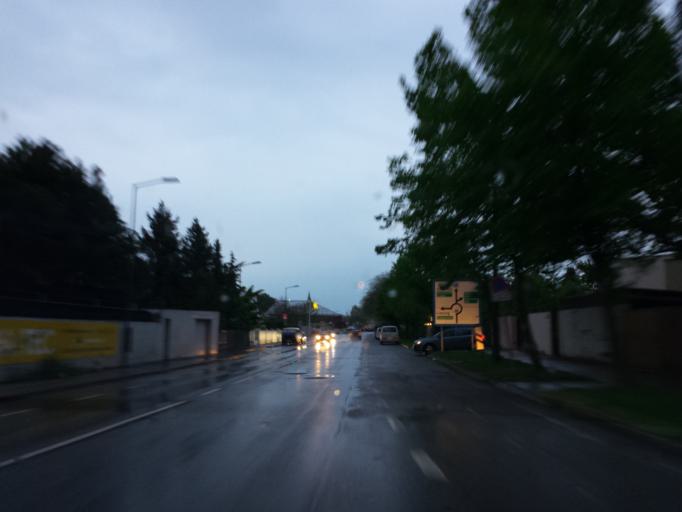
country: AT
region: Lower Austria
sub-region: Politischer Bezirk Modling
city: Perchtoldsdorf
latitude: 48.1257
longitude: 16.2642
